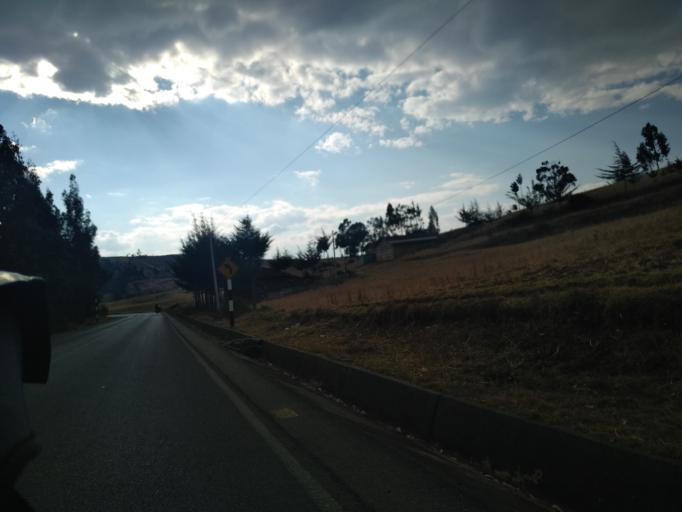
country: PE
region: Cajamarca
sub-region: Provincia de Cajamarca
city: Llacanora
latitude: -7.1436
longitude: -78.4052
